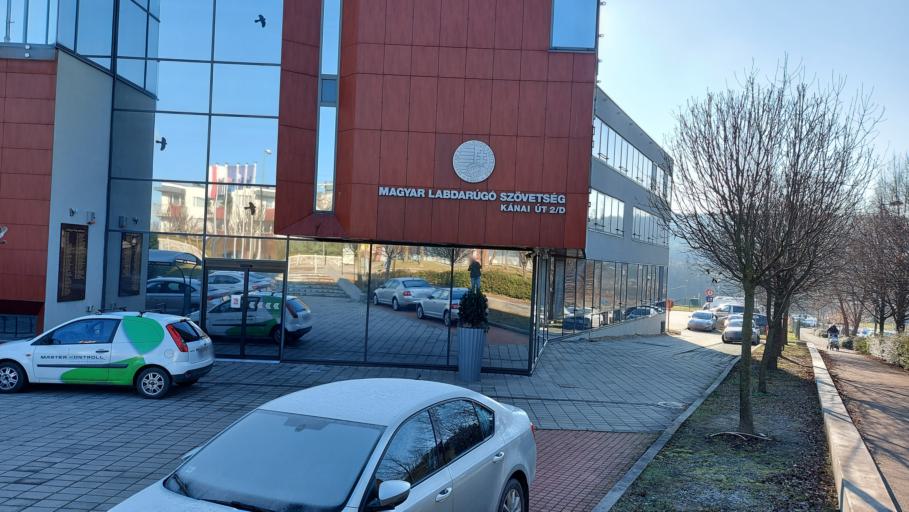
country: HU
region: Pest
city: Budaors
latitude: 47.4475
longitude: 18.9997
